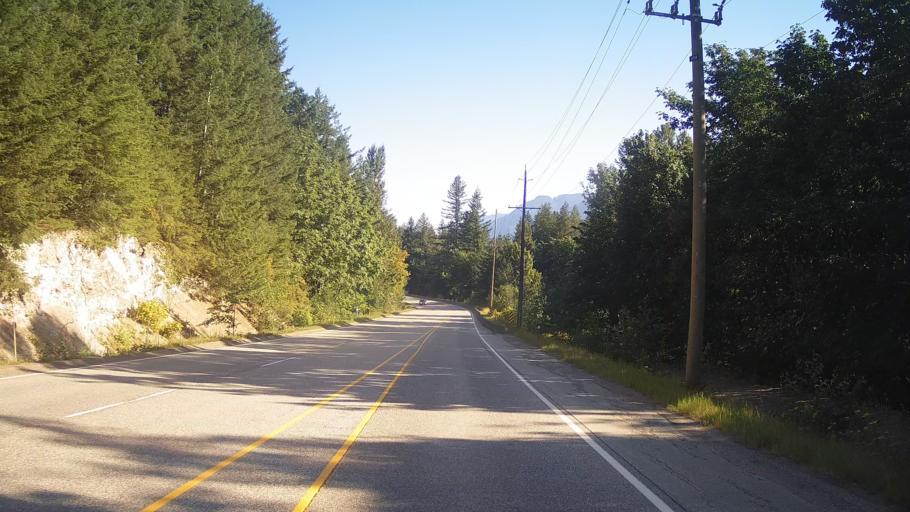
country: CA
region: British Columbia
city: Hope
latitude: 49.4269
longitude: -121.4381
